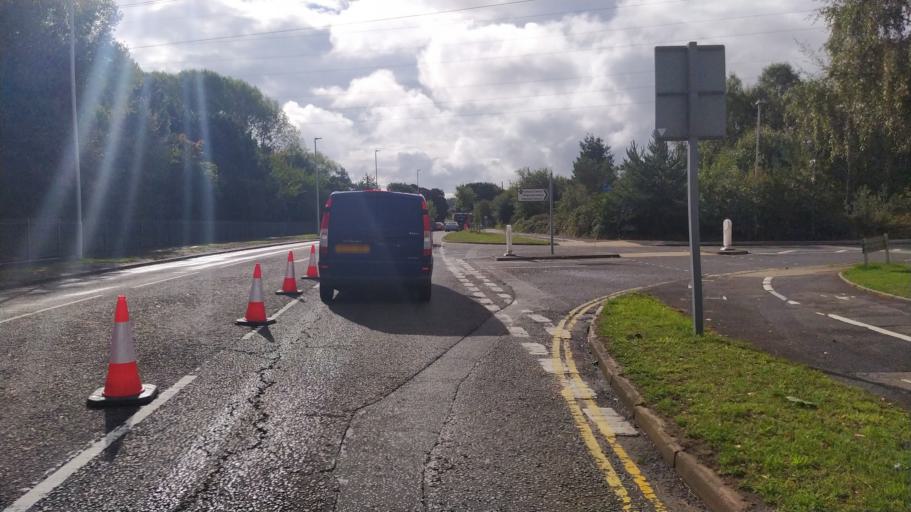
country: GB
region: England
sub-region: Poole
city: Canford Heath
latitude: 50.7484
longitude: -1.9647
